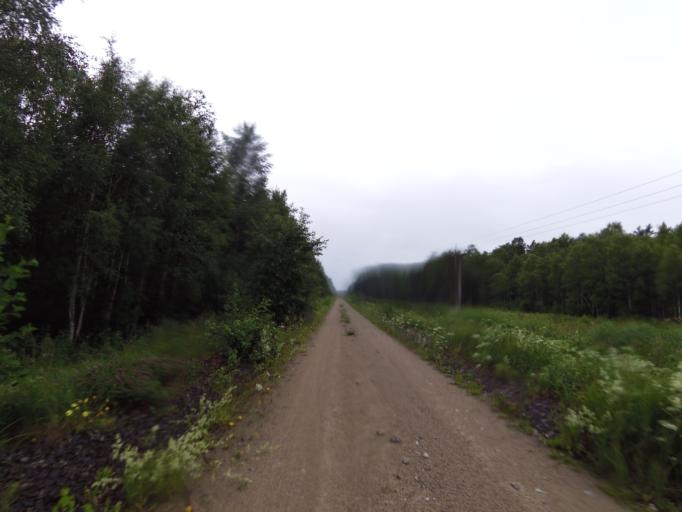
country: EE
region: Laeaene
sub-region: Lihula vald
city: Lihula
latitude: 58.9837
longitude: 23.9244
